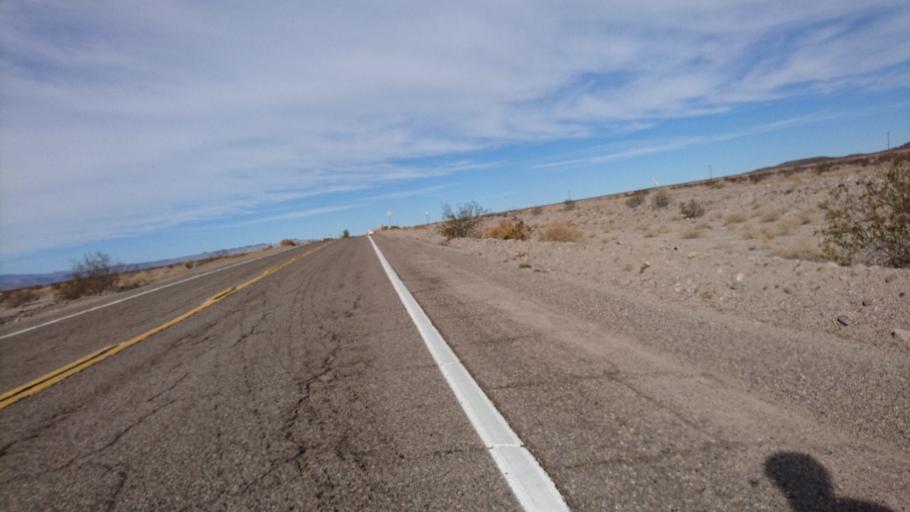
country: US
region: California
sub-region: San Bernardino County
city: Twentynine Palms
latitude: 34.6005
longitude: -115.9475
